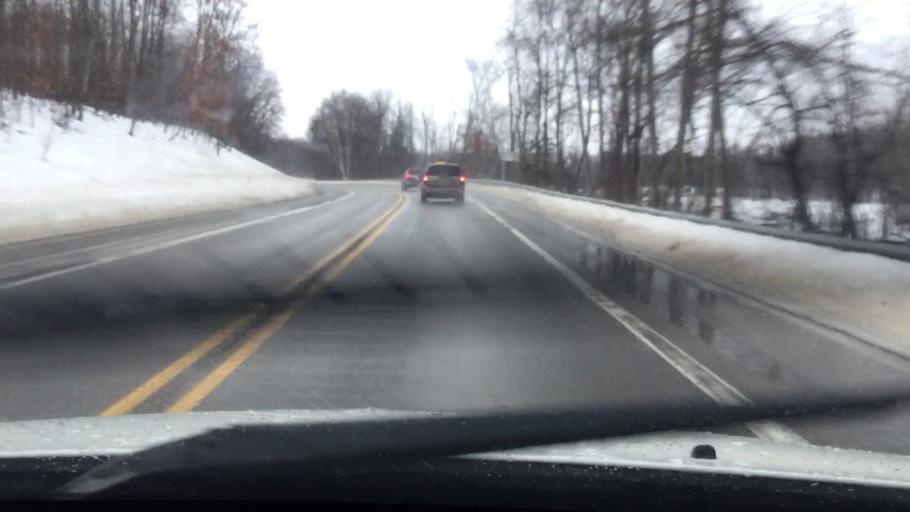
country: US
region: Michigan
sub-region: Charlevoix County
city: East Jordan
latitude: 45.2099
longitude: -85.1693
